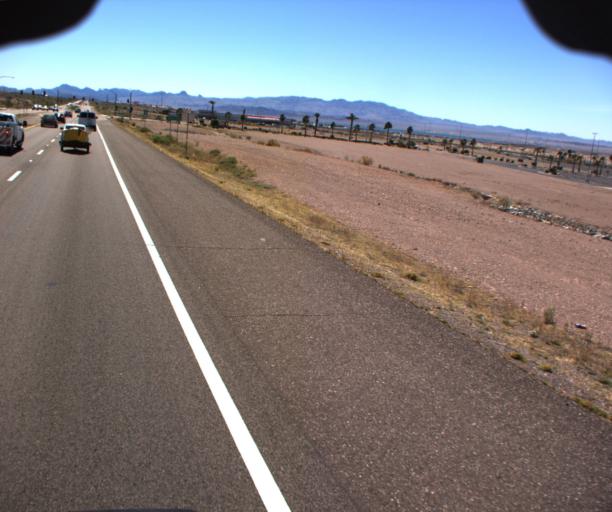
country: US
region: Arizona
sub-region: Mohave County
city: Desert Hills
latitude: 34.5695
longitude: -114.3636
